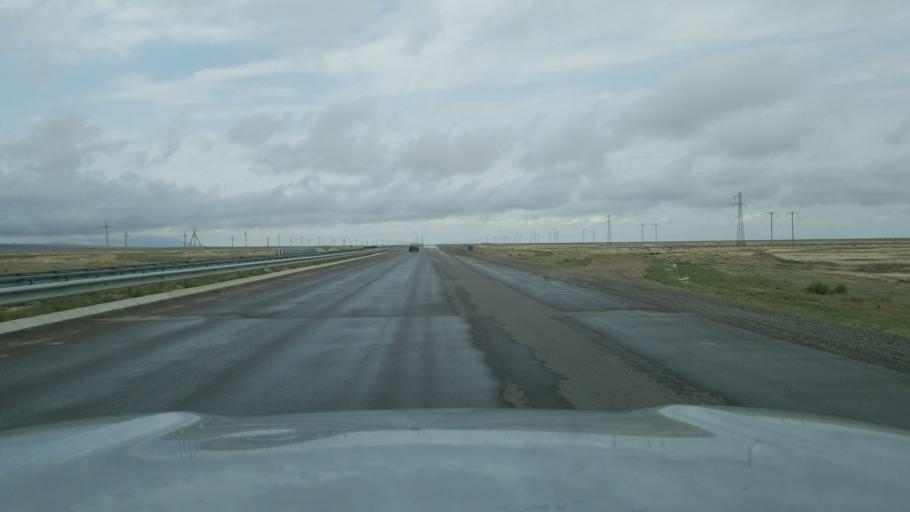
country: TM
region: Balkan
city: Serdar
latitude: 39.1235
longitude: 55.9022
